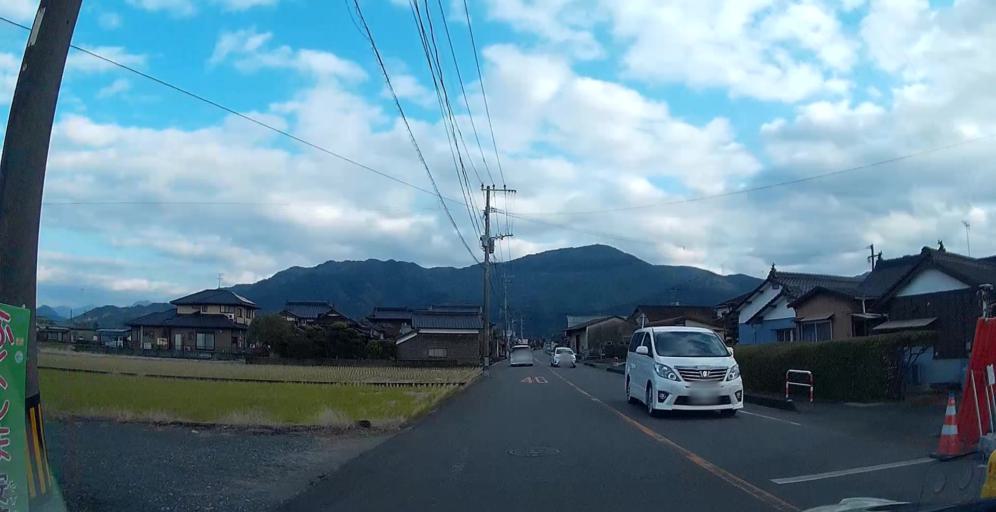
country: JP
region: Kumamoto
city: Yatsushiro
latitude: 32.5355
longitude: 130.6478
